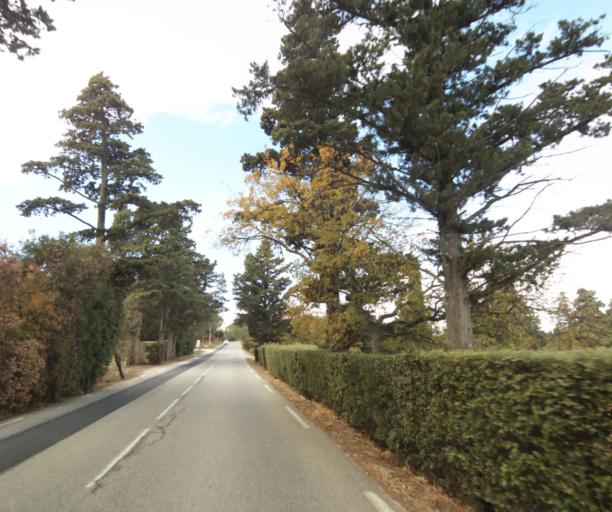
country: FR
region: Provence-Alpes-Cote d'Azur
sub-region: Departement des Bouches-du-Rhone
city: Cuges-les-Pins
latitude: 43.2416
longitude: 5.7035
